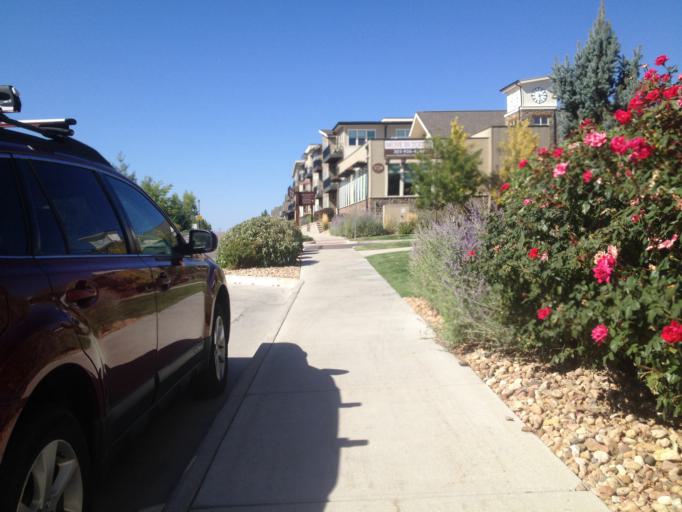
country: US
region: Colorado
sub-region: Boulder County
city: Louisville
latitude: 39.9881
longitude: -105.1321
